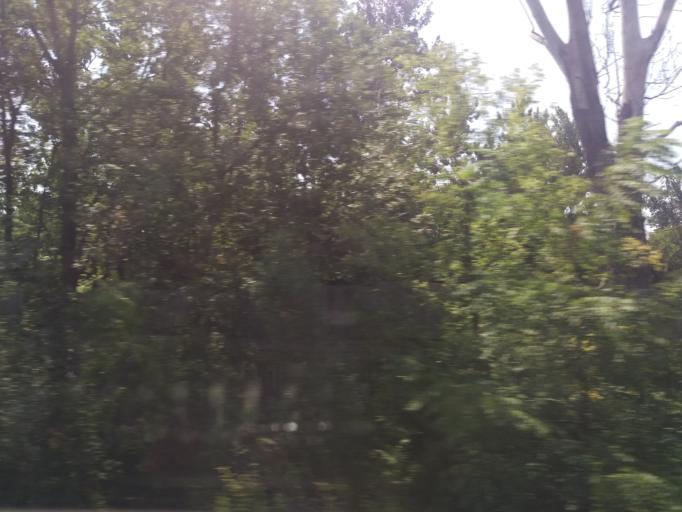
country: CA
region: Ontario
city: Scarborough
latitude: 43.7577
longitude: -79.1840
